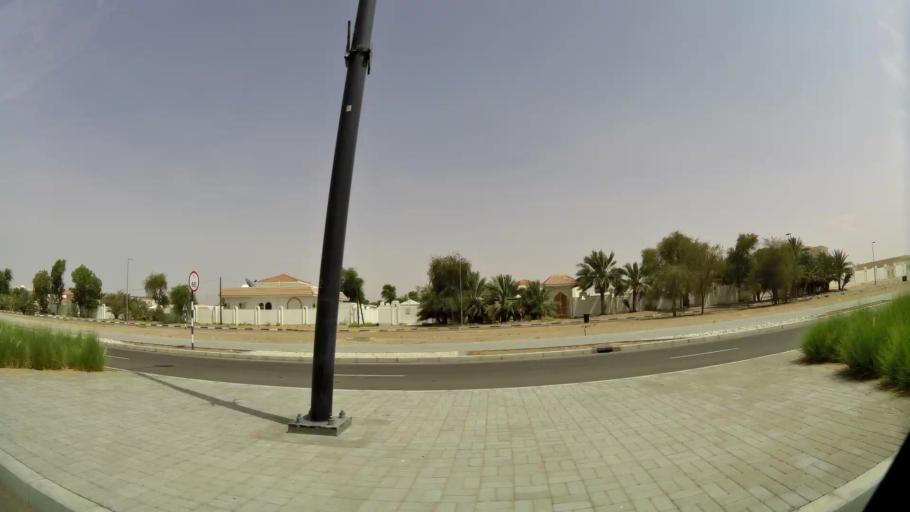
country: AE
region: Abu Dhabi
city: Al Ain
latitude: 24.1411
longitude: 55.6425
